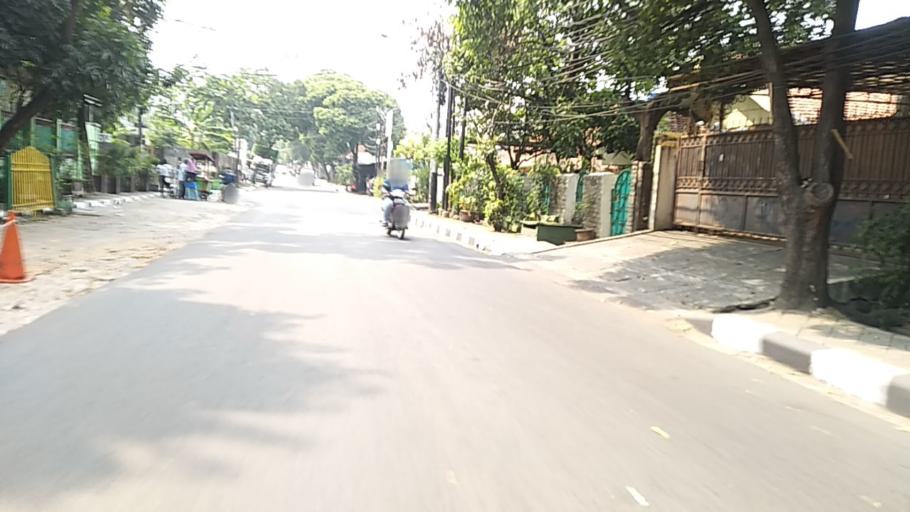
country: ID
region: Jakarta Raya
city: Jakarta
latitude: -6.2339
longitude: 106.8488
